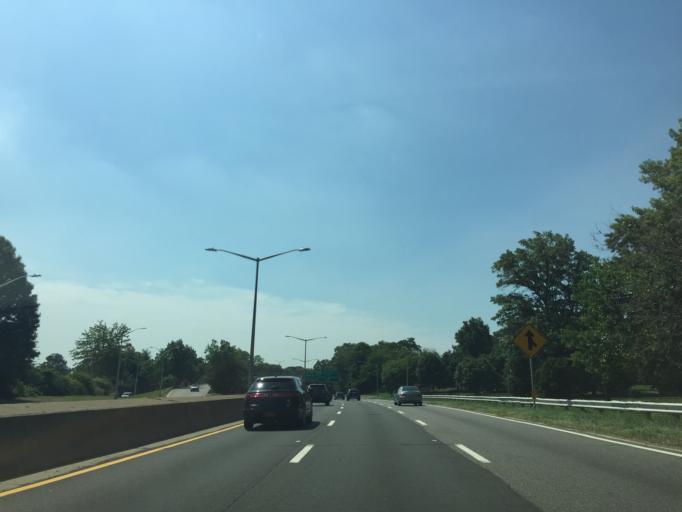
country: US
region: New York
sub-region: Nassau County
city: Bellerose Terrace
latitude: 40.7134
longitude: -73.7291
